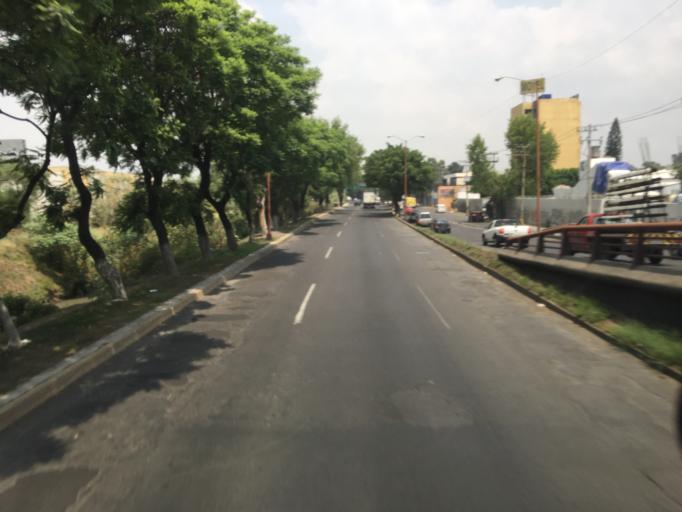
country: MX
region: Mexico
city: Tlalnepantla
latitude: 19.5311
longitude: -99.1727
